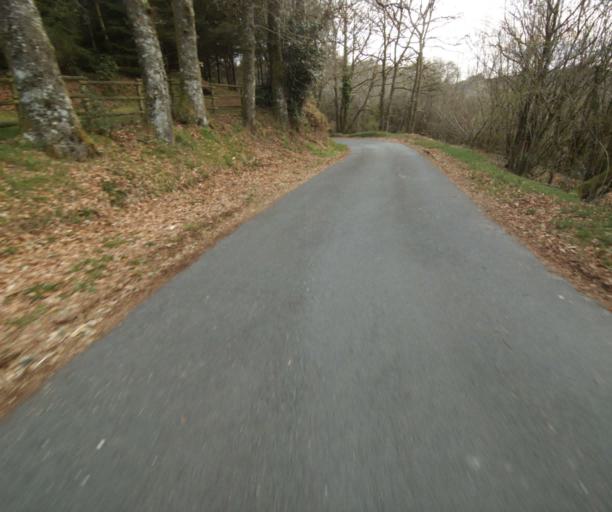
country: FR
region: Limousin
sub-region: Departement de la Correze
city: Correze
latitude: 45.3797
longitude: 1.8852
